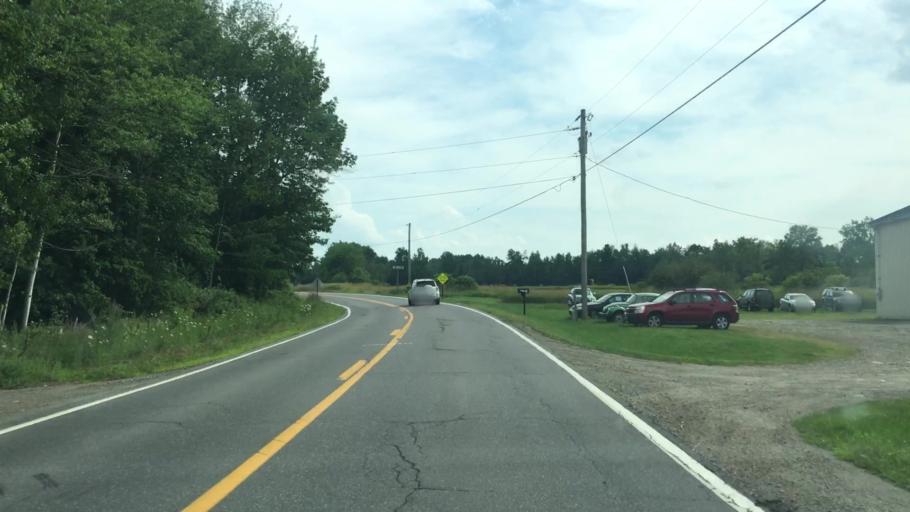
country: US
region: Maine
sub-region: Kennebec County
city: Vassalboro
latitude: 44.4392
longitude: -69.6057
